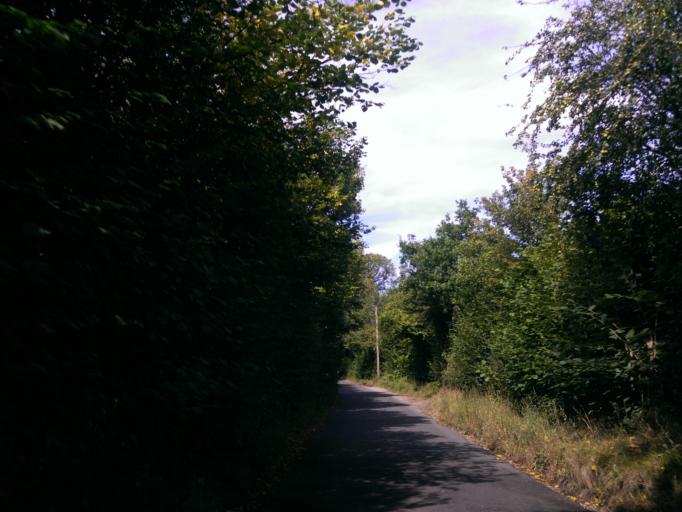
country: GB
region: England
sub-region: Essex
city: Sible Hedingham
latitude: 51.9619
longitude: 0.6296
